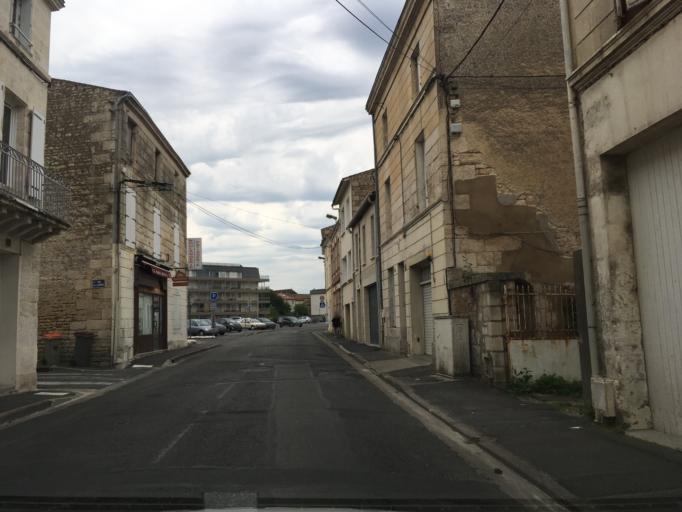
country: FR
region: Poitou-Charentes
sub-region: Departement des Deux-Sevres
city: Niort
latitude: 46.3291
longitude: -0.4691
